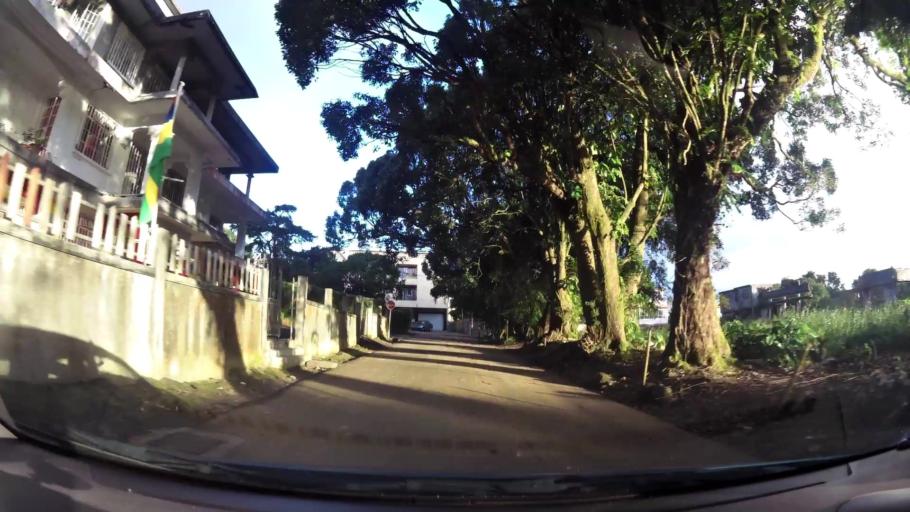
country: MU
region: Plaines Wilhems
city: Curepipe
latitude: -20.3142
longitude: 57.5288
